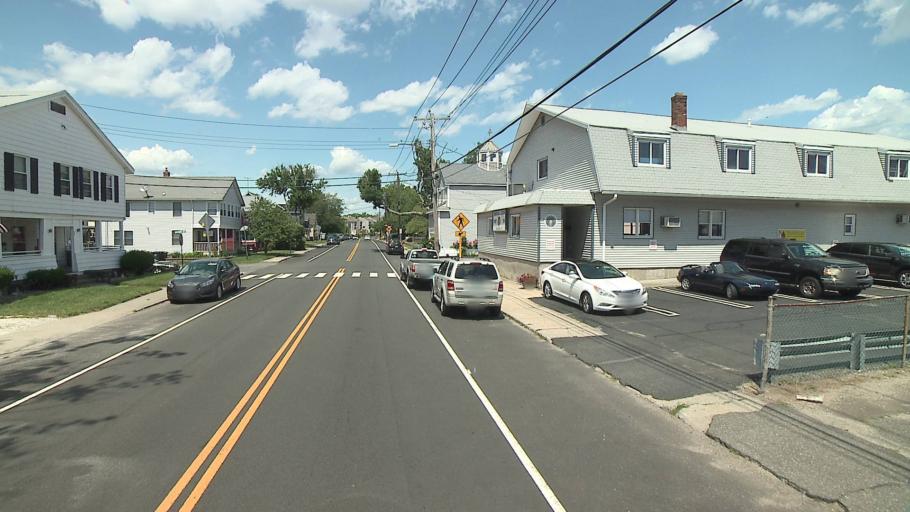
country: US
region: Connecticut
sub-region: New Haven County
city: Woodmont
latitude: 41.2217
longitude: -73.0049
